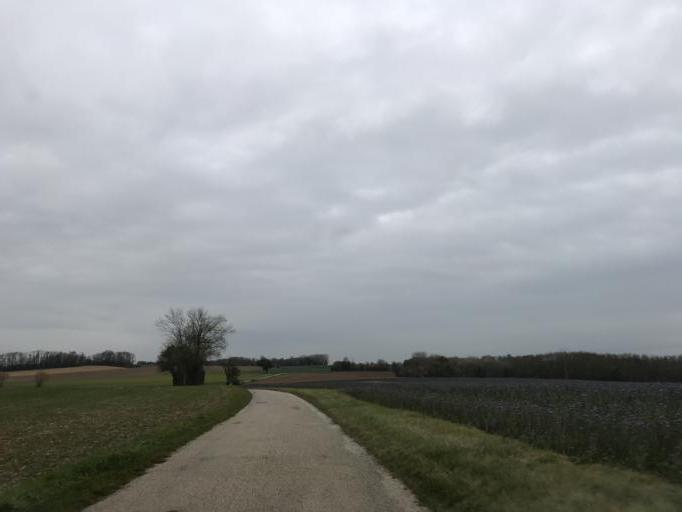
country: FR
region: Rhone-Alpes
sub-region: Departement de l'Ain
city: Saint-Maurice-de-Beynost
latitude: 45.8398
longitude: 4.9680
